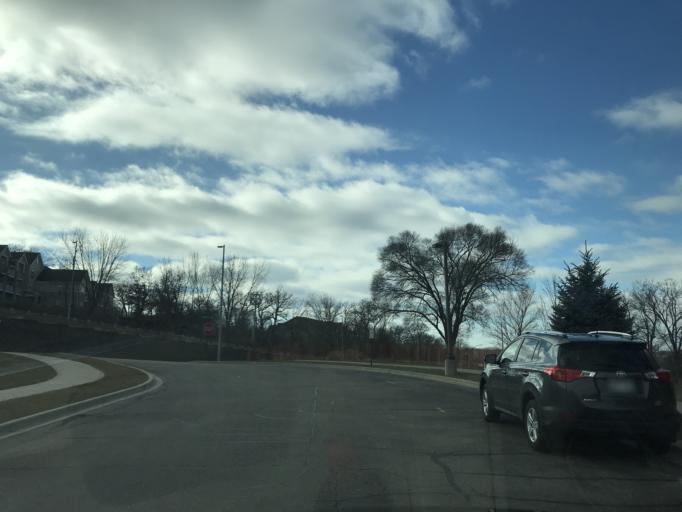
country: US
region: Wisconsin
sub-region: Dane County
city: Monona
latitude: 43.1219
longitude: -89.2946
